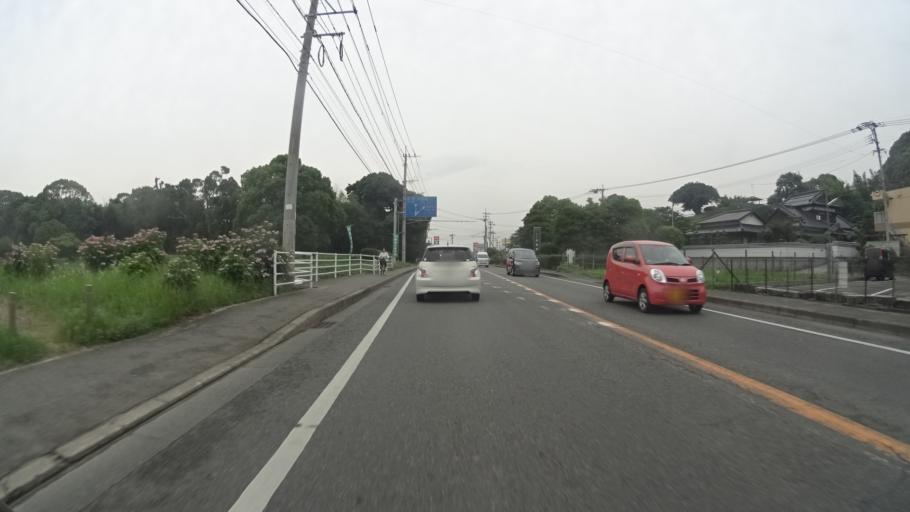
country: JP
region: Fukuoka
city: Onojo
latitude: 33.5211
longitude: 130.4991
